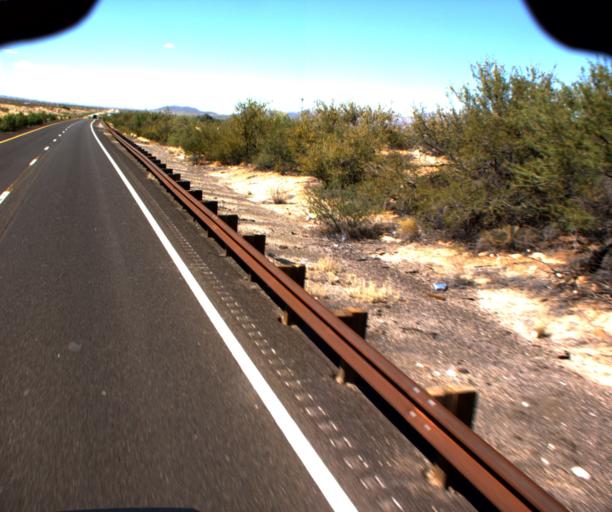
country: US
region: Arizona
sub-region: Yavapai County
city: Bagdad
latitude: 34.8351
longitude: -113.6322
